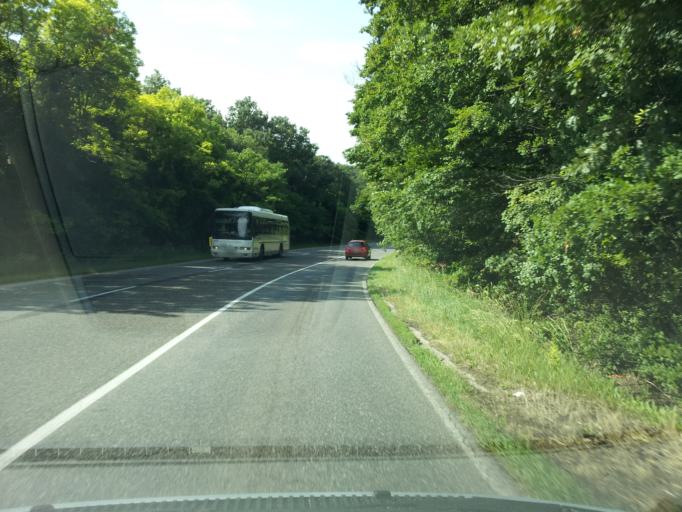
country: HU
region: Veszprem
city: Csopak
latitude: 46.9986
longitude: 17.9160
